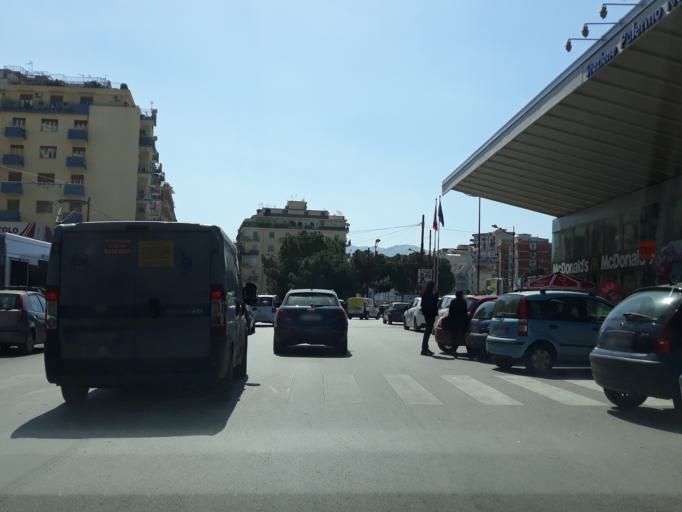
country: IT
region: Sicily
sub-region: Palermo
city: Palermo
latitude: 38.1326
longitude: 13.3421
